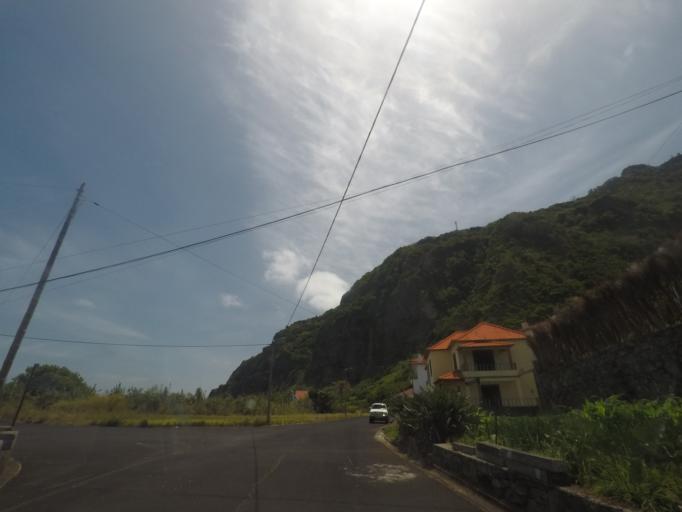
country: PT
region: Madeira
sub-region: Sao Vicente
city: Sao Vicente
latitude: 32.8261
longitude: -16.9890
